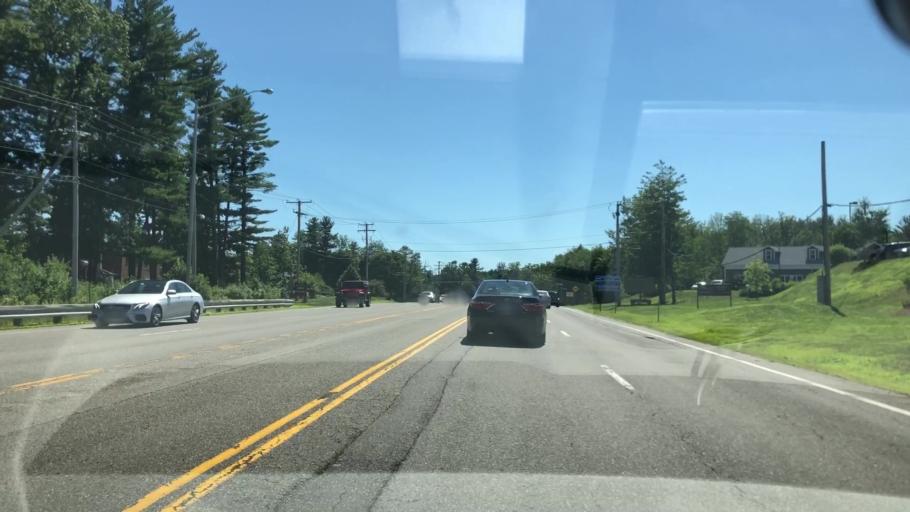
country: US
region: New Hampshire
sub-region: Hillsborough County
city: Bedford
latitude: 42.9586
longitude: -71.5039
